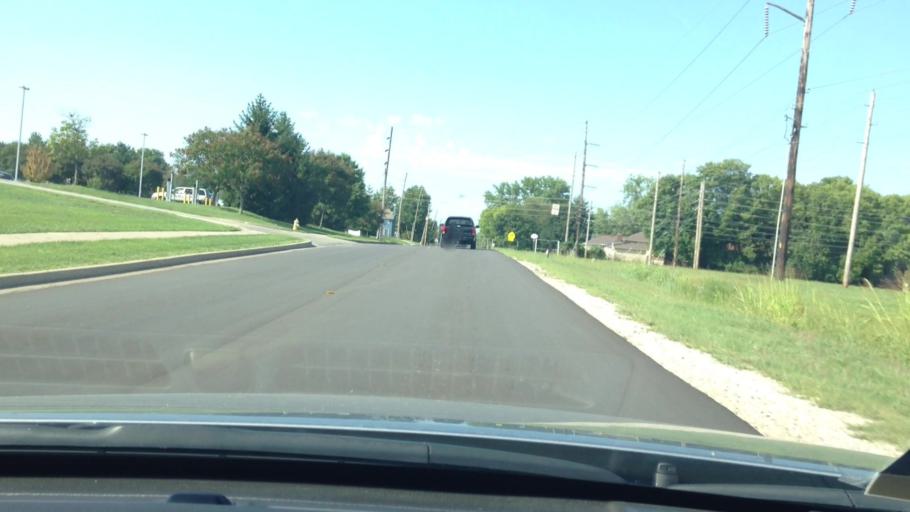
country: US
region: Missouri
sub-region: Jackson County
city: Grandview
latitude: 38.8773
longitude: -94.5080
